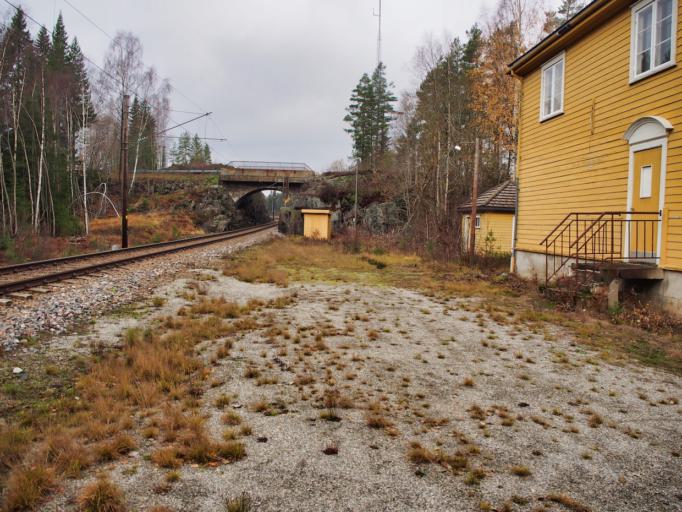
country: NO
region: Aust-Agder
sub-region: Vegarshei
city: Myra
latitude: 58.7846
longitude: 8.9366
